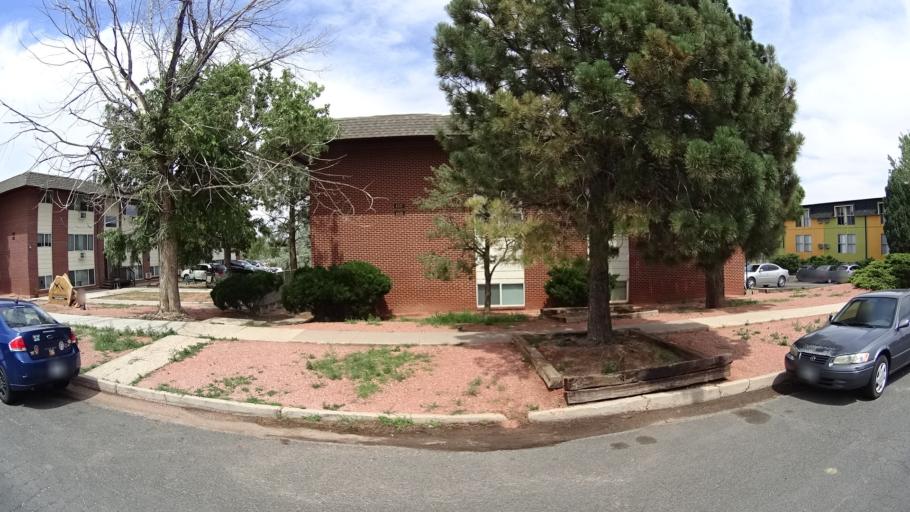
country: US
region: Colorado
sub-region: El Paso County
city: Colorado Springs
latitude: 38.8925
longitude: -104.8346
